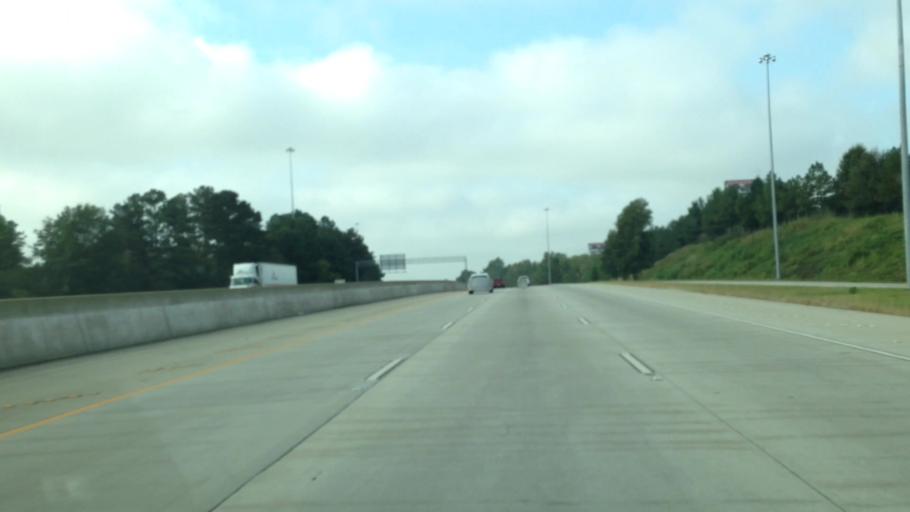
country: US
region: Georgia
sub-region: Coweta County
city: Newnan
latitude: 33.3953
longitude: -84.7505
